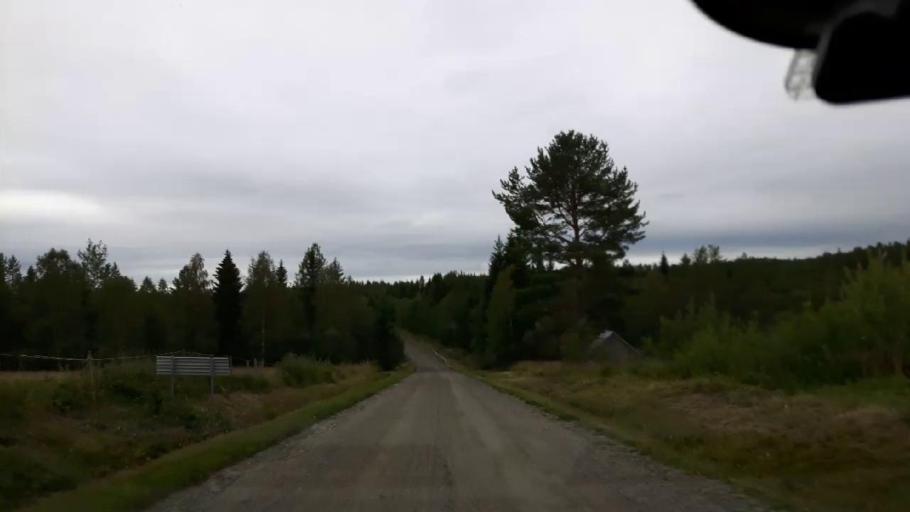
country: SE
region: Vaesternorrland
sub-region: Ange Kommun
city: Fransta
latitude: 62.8656
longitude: 15.9848
